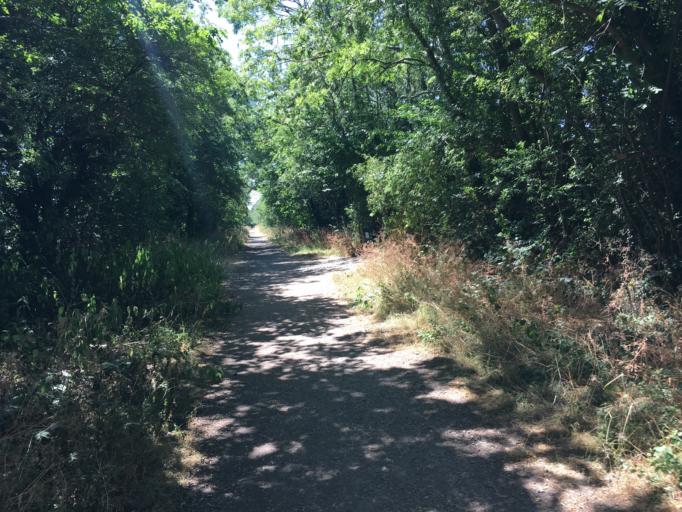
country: GB
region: England
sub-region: Warwickshire
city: Rugby
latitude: 52.3953
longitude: -1.2313
